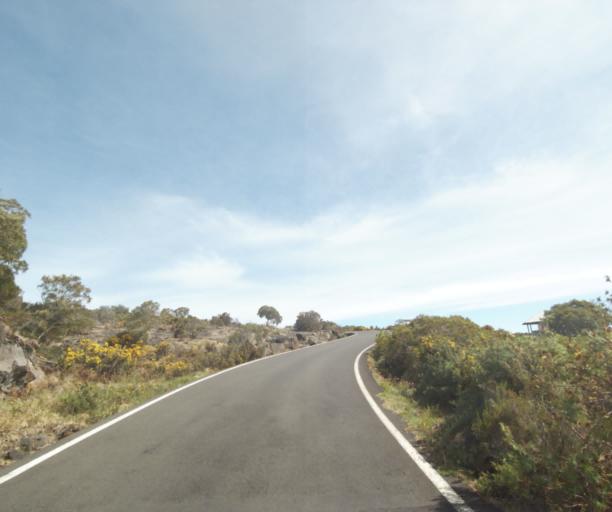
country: RE
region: Reunion
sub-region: Reunion
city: Trois-Bassins
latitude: -21.0681
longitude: 55.3786
